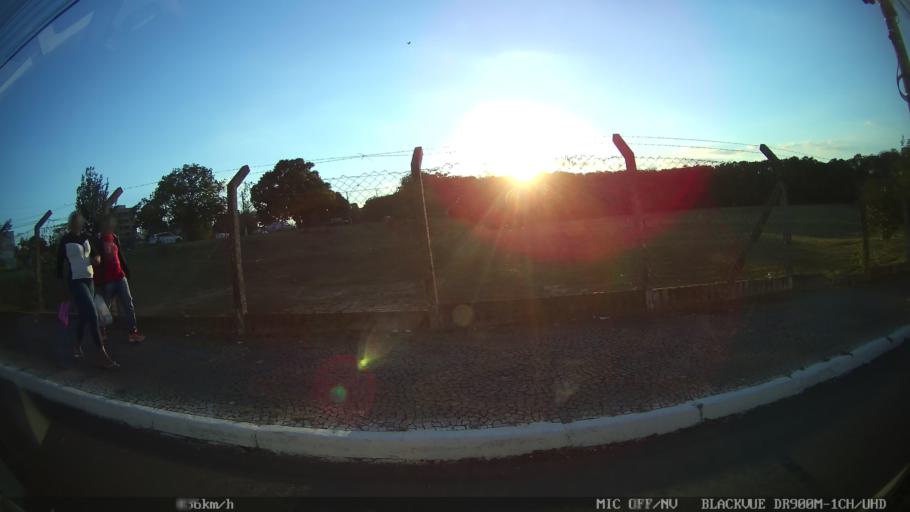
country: BR
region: Sao Paulo
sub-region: Santa Barbara D'Oeste
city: Santa Barbara d'Oeste
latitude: -22.7482
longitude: -47.4106
